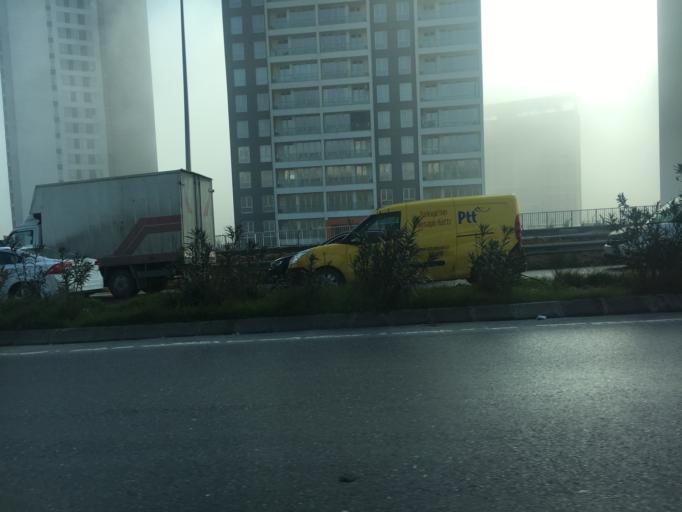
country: TR
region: Istanbul
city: Esenyurt
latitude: 41.0543
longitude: 28.6843
